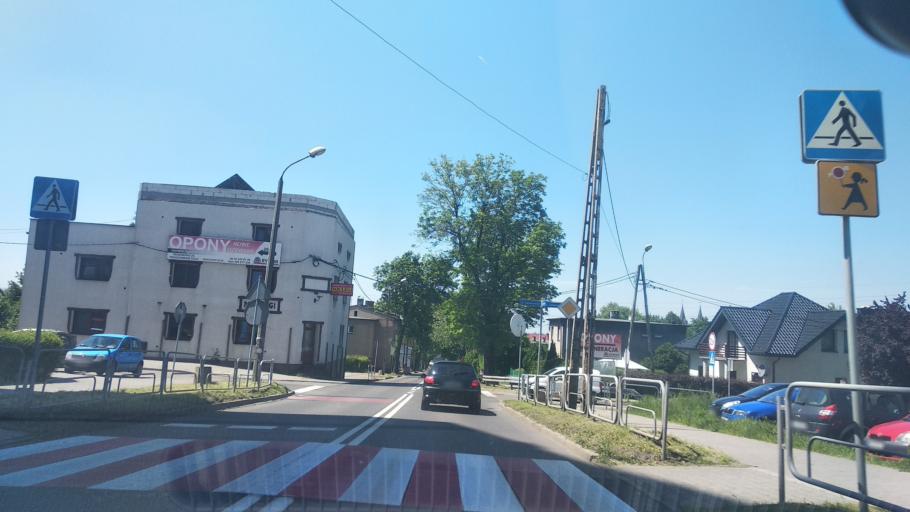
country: PL
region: Silesian Voivodeship
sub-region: Swietochlowice
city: Swietochlowice
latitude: 50.2522
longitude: 18.9092
